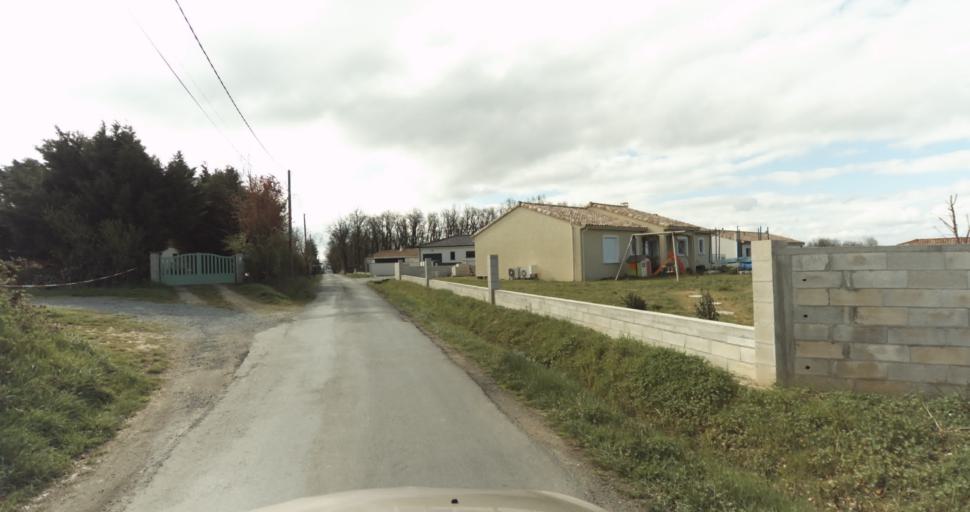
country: FR
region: Midi-Pyrenees
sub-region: Departement du Tarn
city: Frejairolles
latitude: 43.8656
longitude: 2.2057
